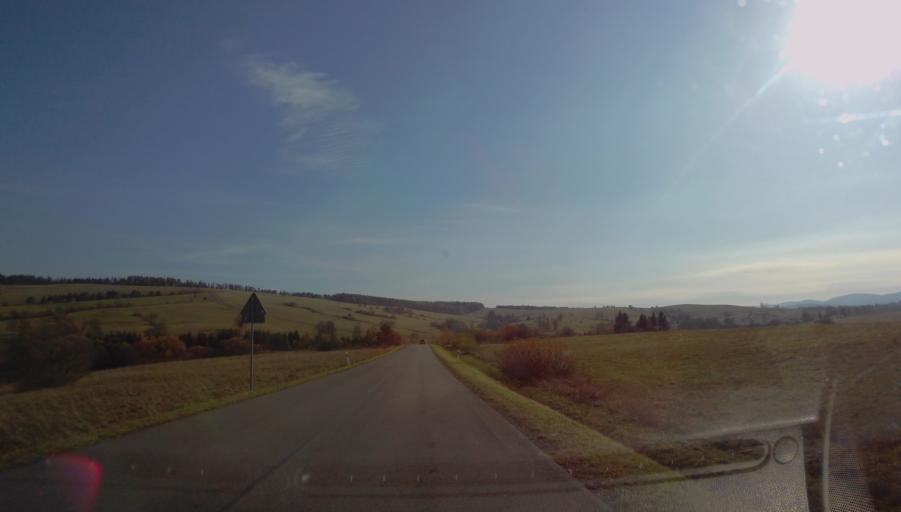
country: PL
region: Subcarpathian Voivodeship
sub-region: Powiat sanocki
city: Komancza
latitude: 49.2848
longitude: 22.0693
